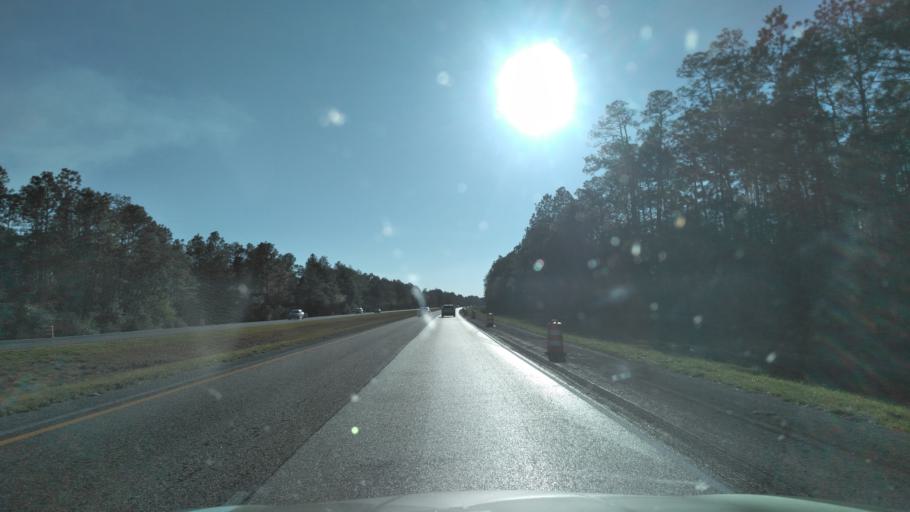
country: US
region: Alabama
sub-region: Baldwin County
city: Bay Minette
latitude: 30.9784
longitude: -87.7170
